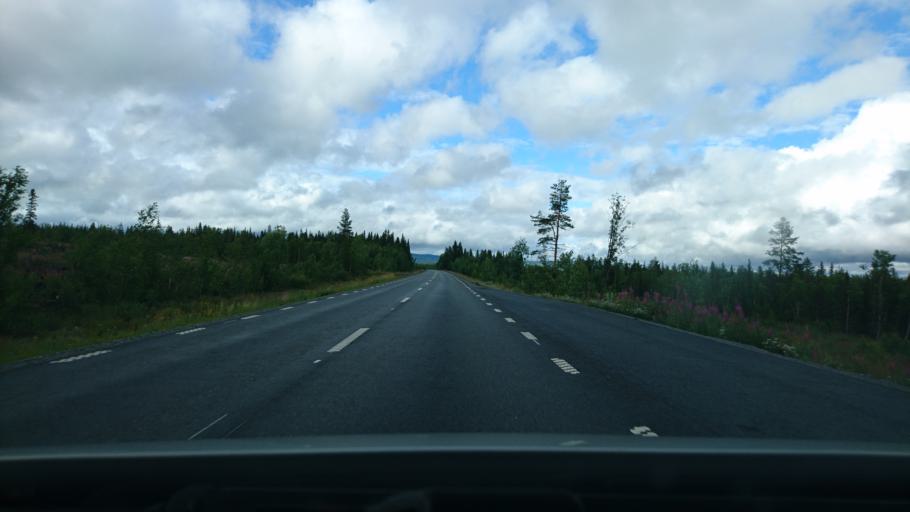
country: SE
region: Vaesterbotten
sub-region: Vilhelmina Kommun
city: Vilhelmina
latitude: 64.7789
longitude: 16.7639
